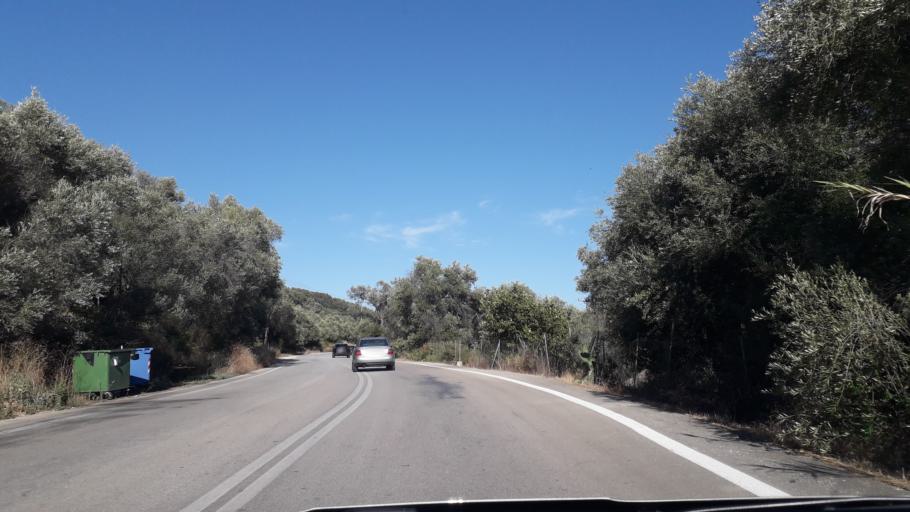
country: GR
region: Ionian Islands
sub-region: Nomos Kerkyras
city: Perivoli
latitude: 39.4433
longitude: 19.9498
